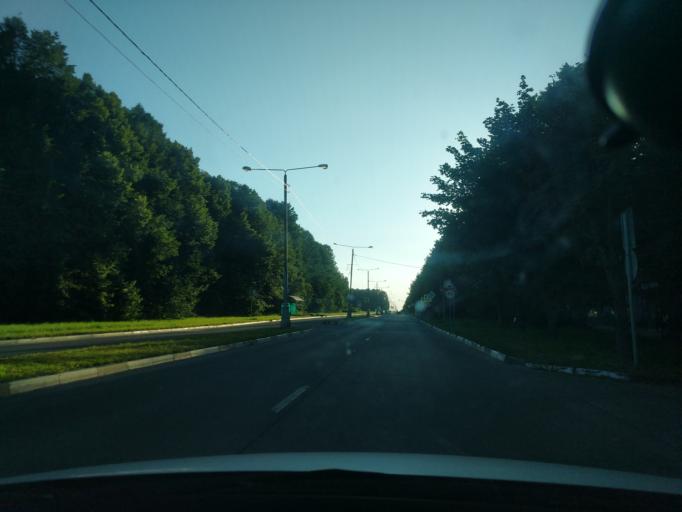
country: RU
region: Moskovskaya
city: Pushchino
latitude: 54.8327
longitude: 37.6184
